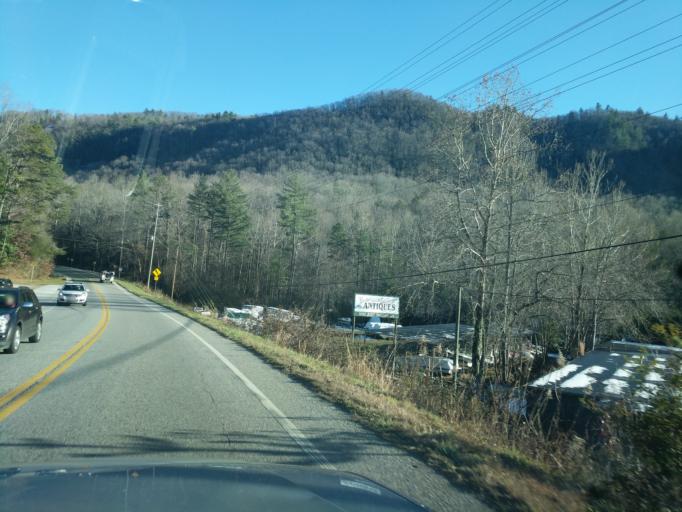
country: US
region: Georgia
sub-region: Rabun County
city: Clayton
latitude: 34.8599
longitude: -83.5121
